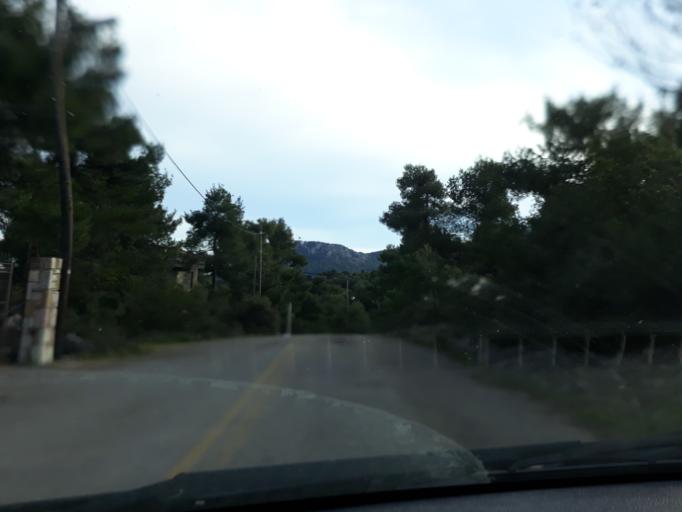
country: GR
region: Attica
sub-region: Nomarchia Anatolikis Attikis
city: Afidnes
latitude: 38.2144
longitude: 23.7974
